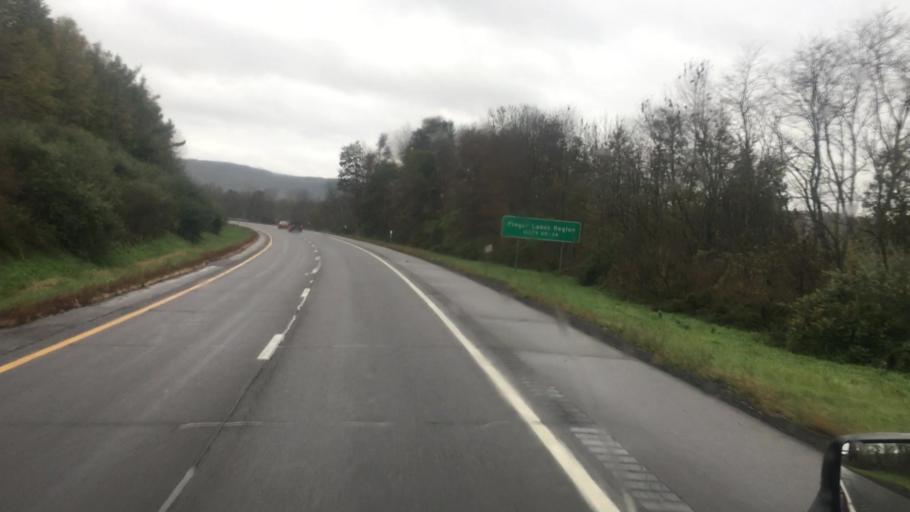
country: US
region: New York
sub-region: Tioga County
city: Apalachin
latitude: 42.0916
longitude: -76.1782
